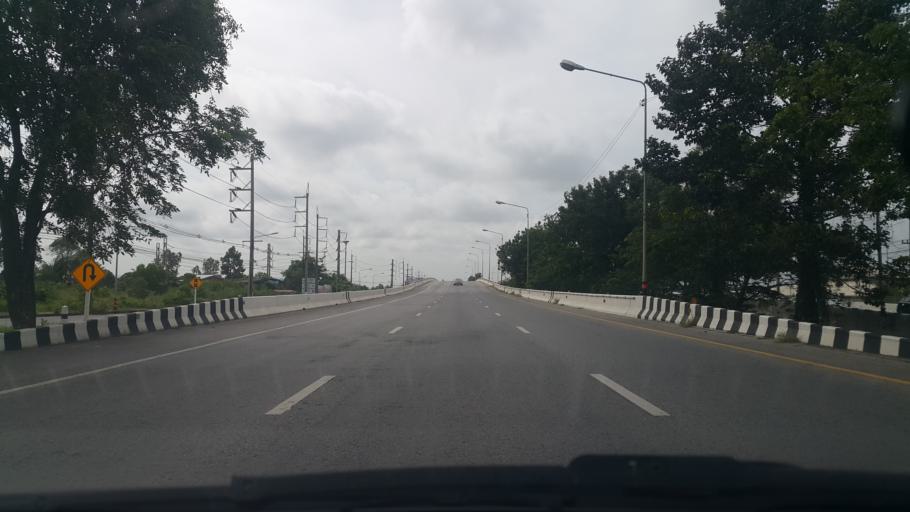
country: TH
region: Rayong
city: Rayong
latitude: 12.6814
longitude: 101.3005
